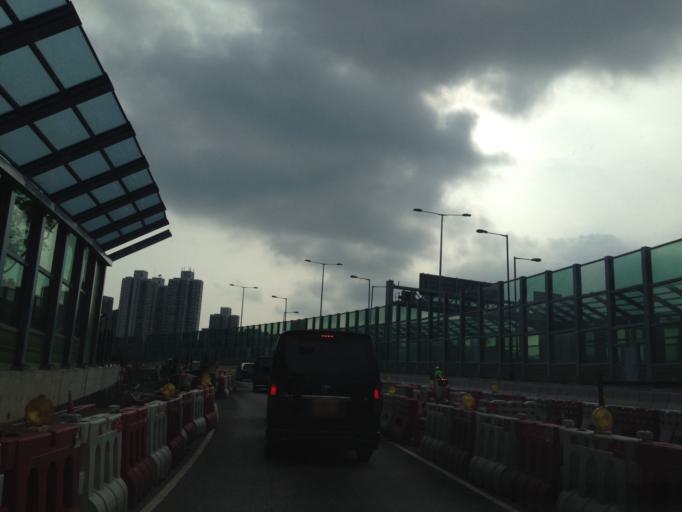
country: HK
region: Tai Po
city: Tai Po
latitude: 22.4447
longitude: 114.1753
